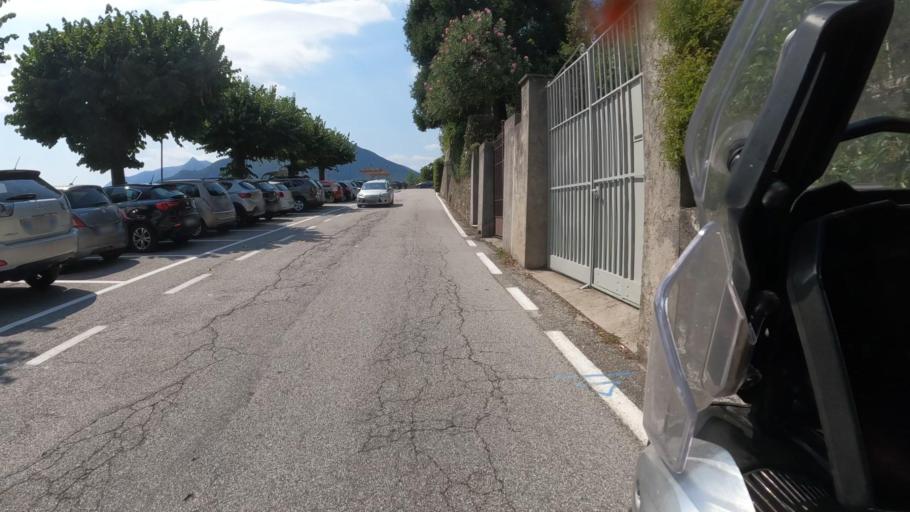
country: IT
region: Lombardy
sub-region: Provincia di Varese
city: Maccagno
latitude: 46.0449
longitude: 8.7417
